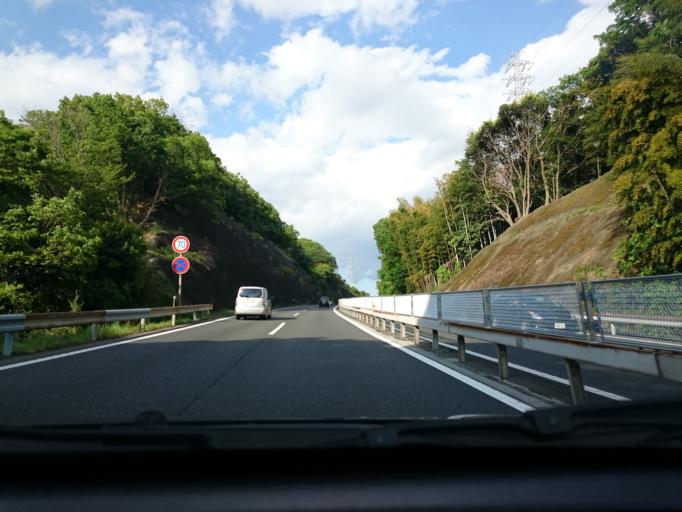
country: JP
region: Kanagawa
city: Oiso
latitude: 35.3252
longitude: 139.2822
